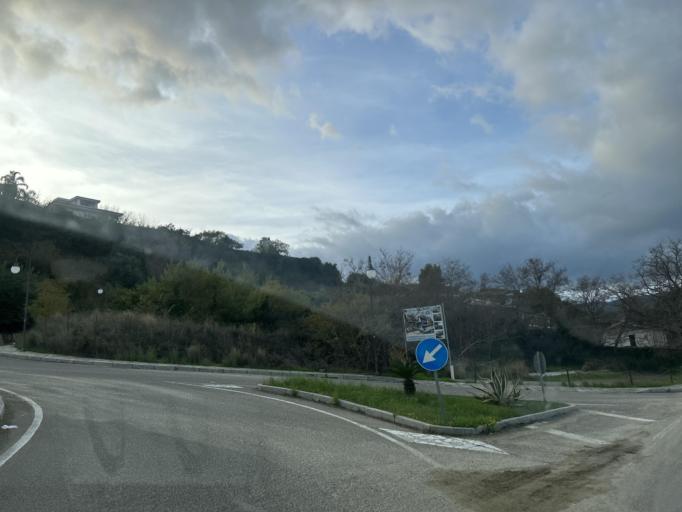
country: IT
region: Calabria
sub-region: Provincia di Catanzaro
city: Soverato Superiore
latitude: 38.7003
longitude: 16.5379
